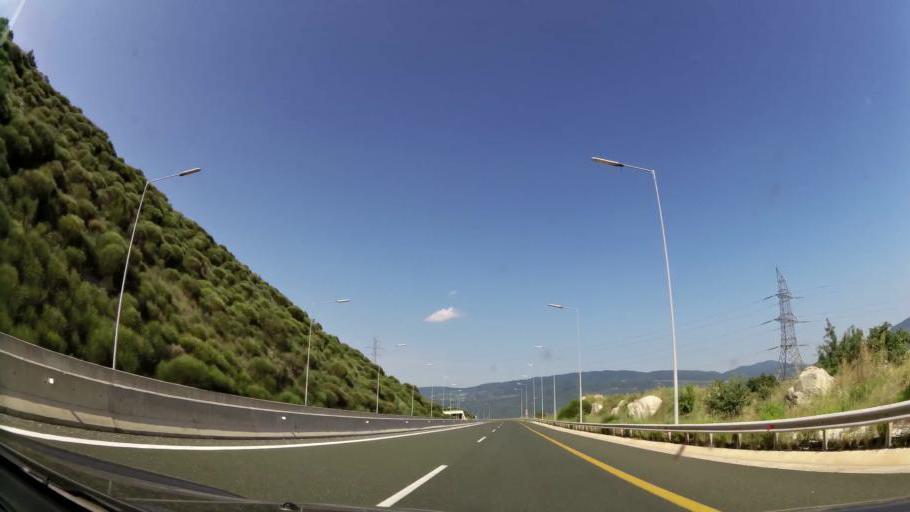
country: GR
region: Central Macedonia
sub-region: Nomos Imathias
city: Rizomata
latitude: 40.3894
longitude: 22.1510
